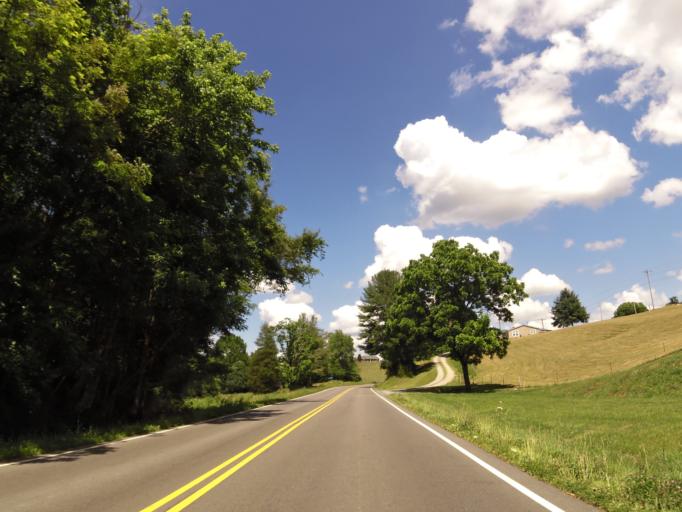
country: US
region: Virginia
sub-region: Lee County
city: Jonesville
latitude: 36.6923
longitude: -83.0758
